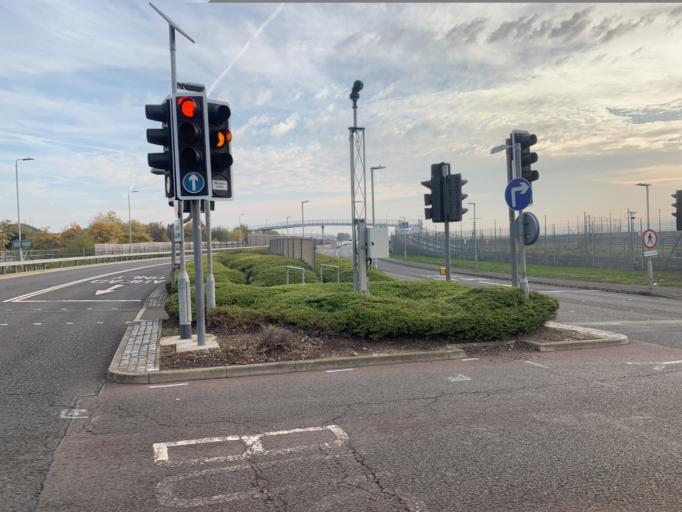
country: GB
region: England
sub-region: Buckinghamshire
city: Iver
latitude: 51.4783
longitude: -0.4936
